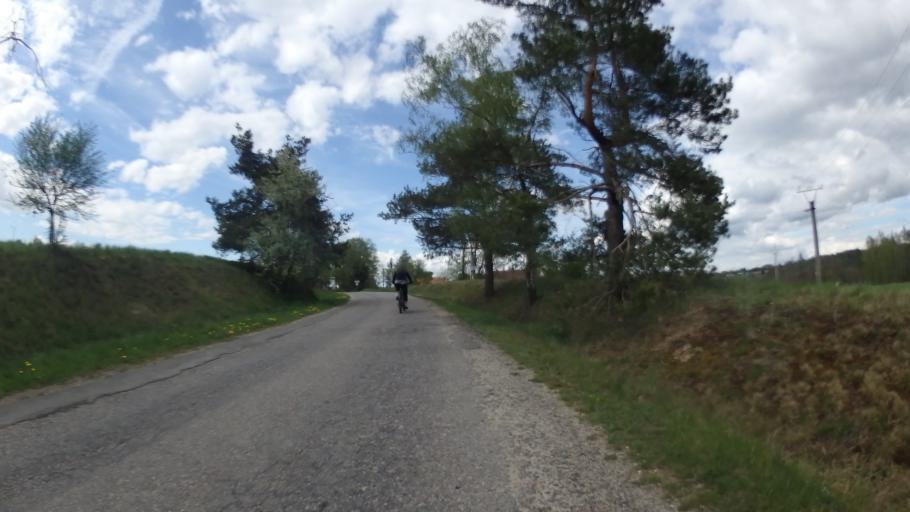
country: CZ
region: Vysocina
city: Merin
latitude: 49.3558
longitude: 15.9360
